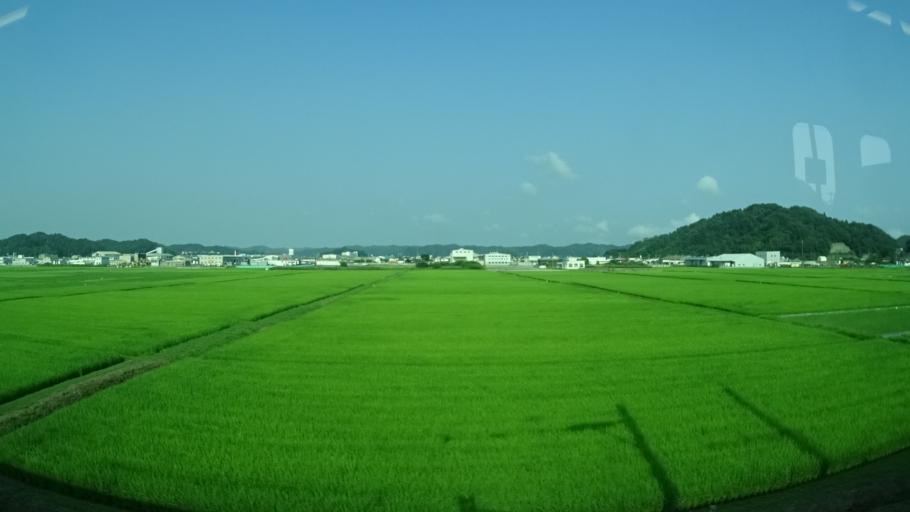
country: JP
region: Fukushima
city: Iwaki
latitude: 36.9750
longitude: 140.8643
